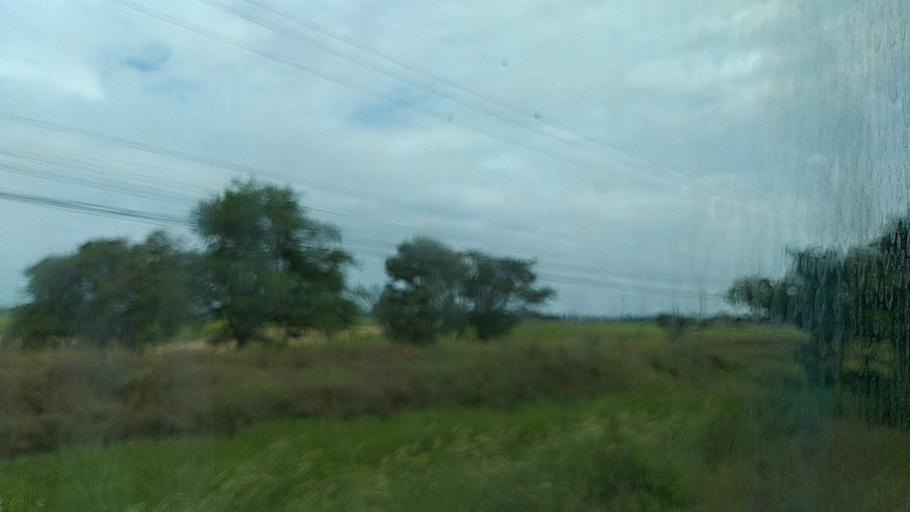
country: TH
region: Roi Et
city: Si Somdet
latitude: 16.1247
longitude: 103.4767
